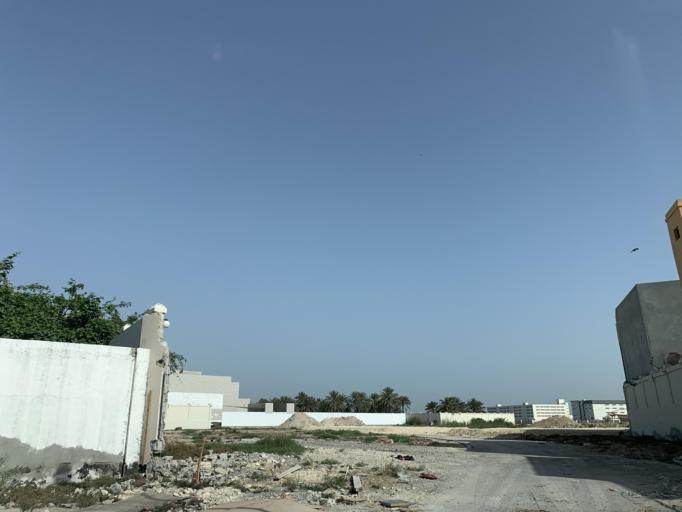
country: BH
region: Northern
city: Sitrah
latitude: 26.1470
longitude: 50.6111
